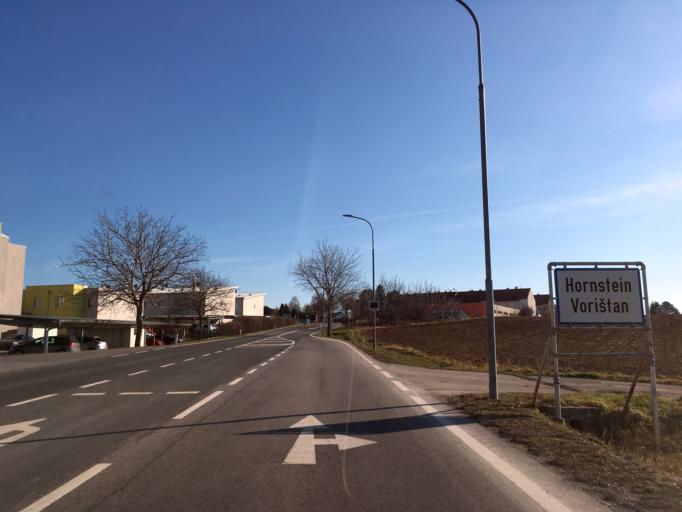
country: AT
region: Burgenland
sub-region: Eisenstadt-Umgebung
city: Hornstein
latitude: 47.8886
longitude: 16.4387
